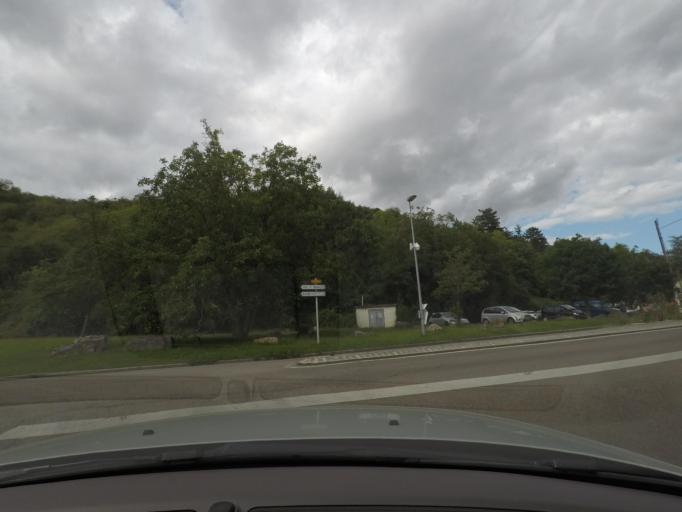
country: FR
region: Haute-Normandie
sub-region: Departement de l'Eure
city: Les Andelys
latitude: 49.2456
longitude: 1.3971
